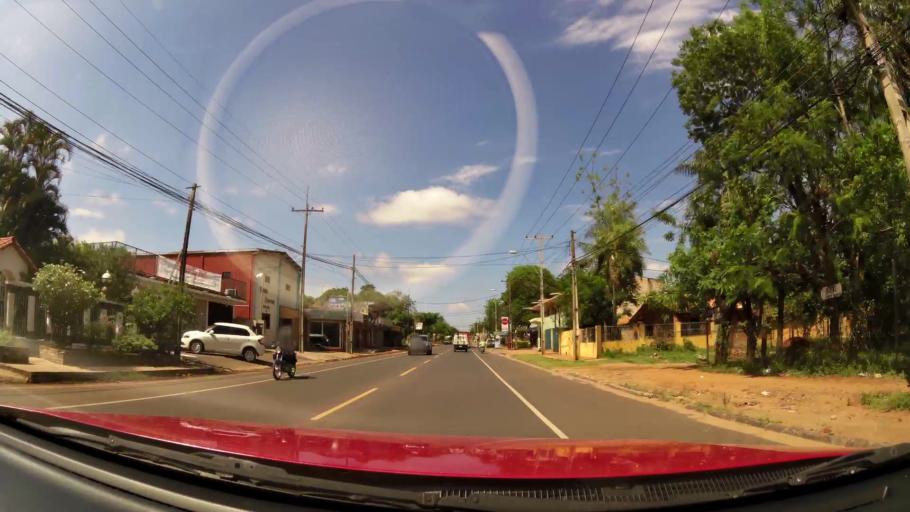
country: PY
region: Central
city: San Lorenzo
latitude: -25.2812
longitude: -57.4984
